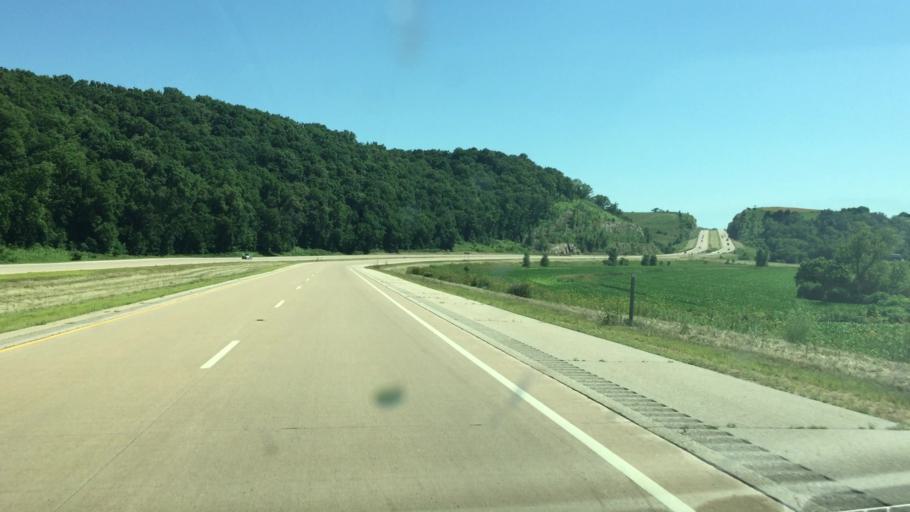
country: US
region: Wisconsin
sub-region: Grant County
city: Dickeyville
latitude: 42.6522
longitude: -90.5746
